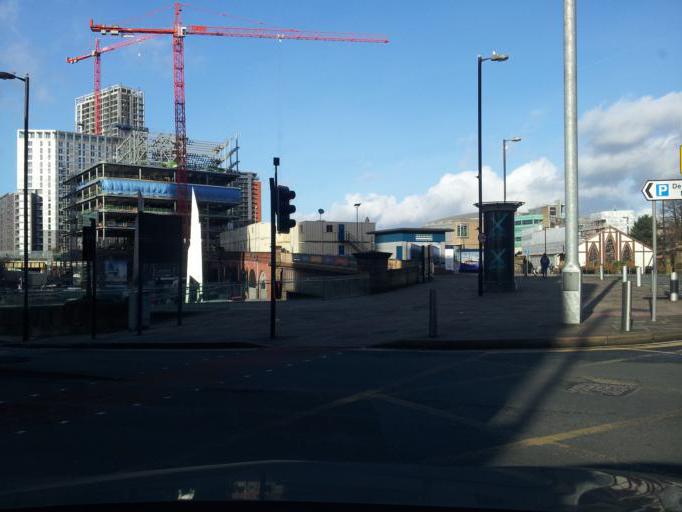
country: GB
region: England
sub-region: Manchester
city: Manchester
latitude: 53.4845
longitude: -2.2453
